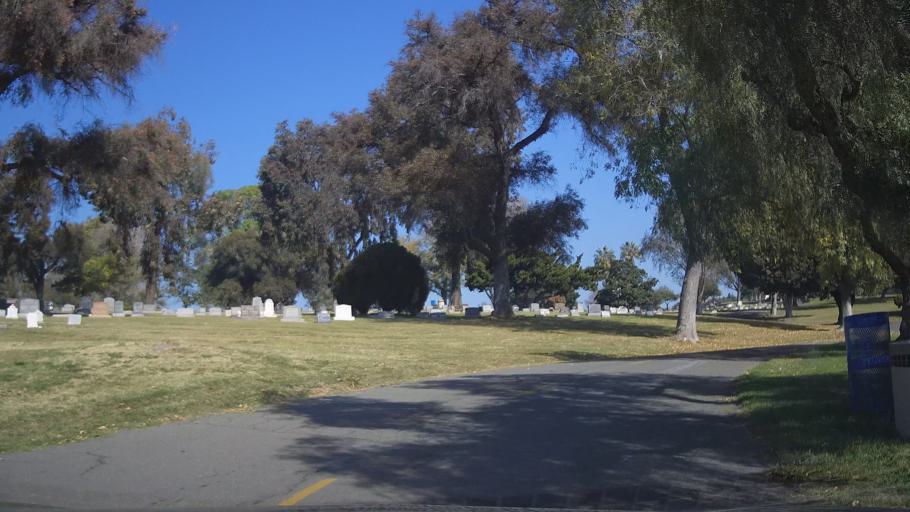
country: US
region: California
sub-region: San Diego County
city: National City
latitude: 32.7068
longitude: -117.1143
